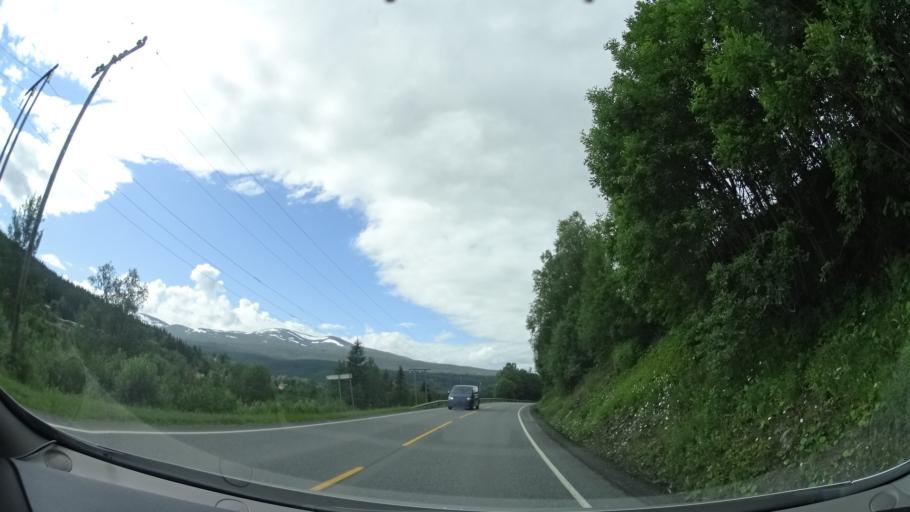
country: NO
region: Nord-Trondelag
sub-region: Meraker
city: Meraker
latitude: 63.4058
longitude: 11.7552
